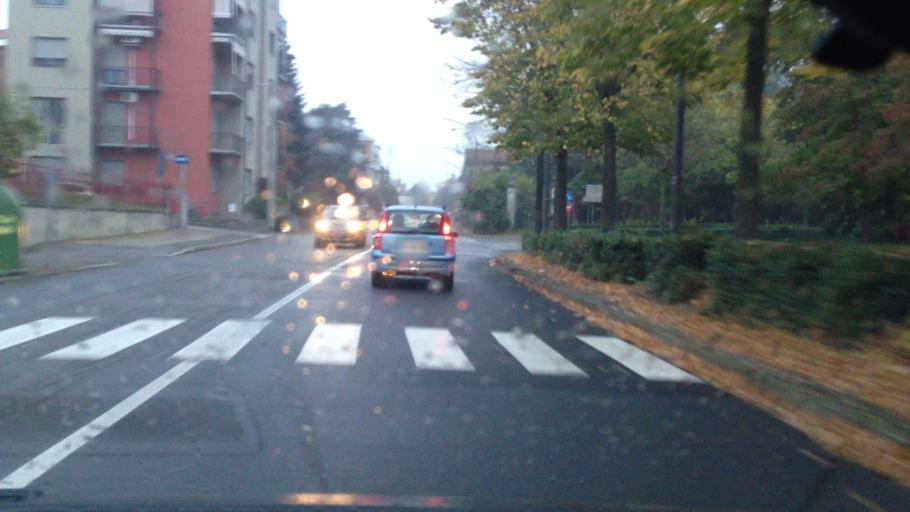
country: IT
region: Piedmont
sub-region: Provincia di Asti
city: Asti
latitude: 44.9122
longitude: 8.1994
